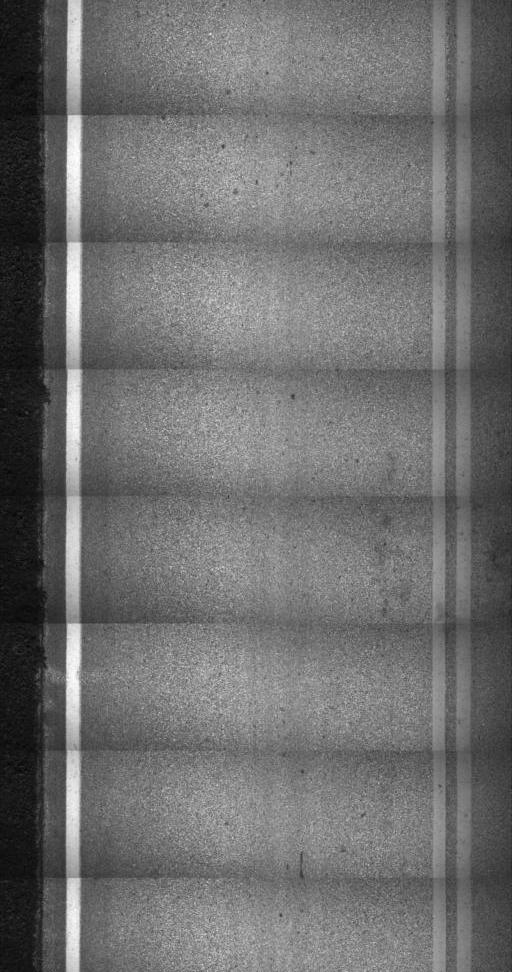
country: US
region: Vermont
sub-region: Rutland County
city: Poultney
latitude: 43.4916
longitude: -73.2382
